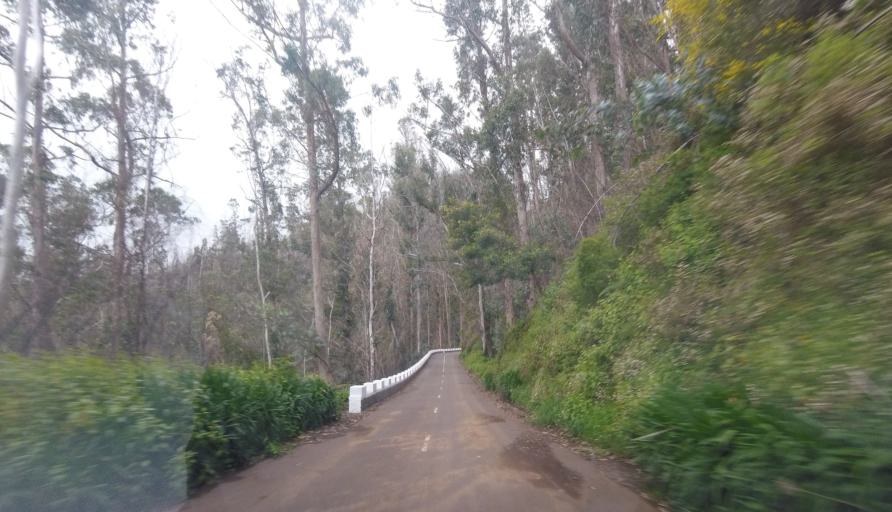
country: PT
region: Madeira
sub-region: Funchal
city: Nossa Senhora do Monte
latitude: 32.6887
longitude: -16.8896
